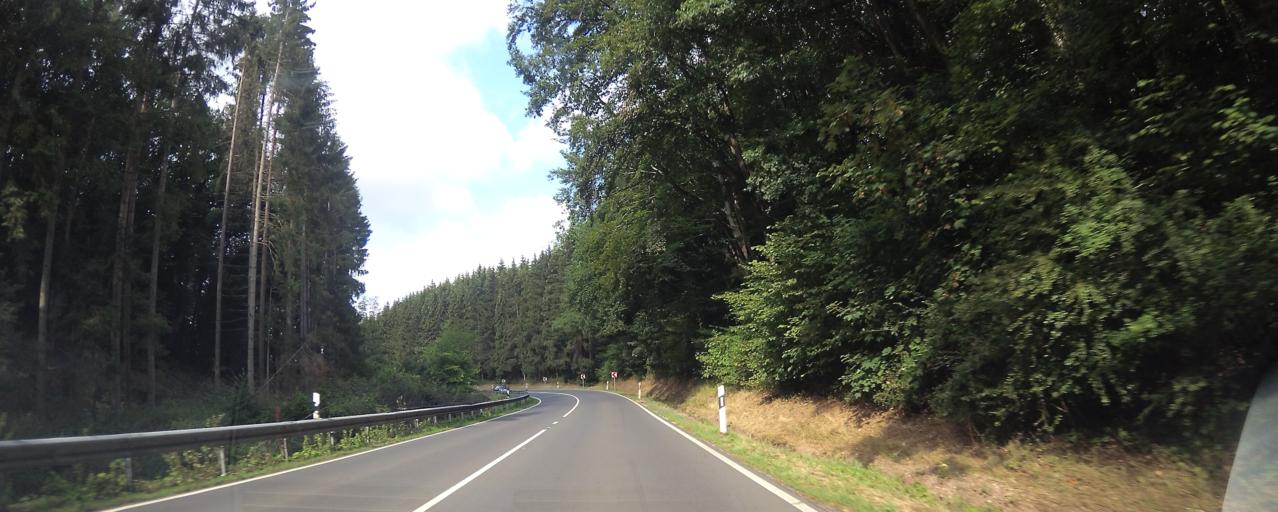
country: DE
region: Rheinland-Pfalz
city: Beilingen
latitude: 49.9684
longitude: 6.6682
